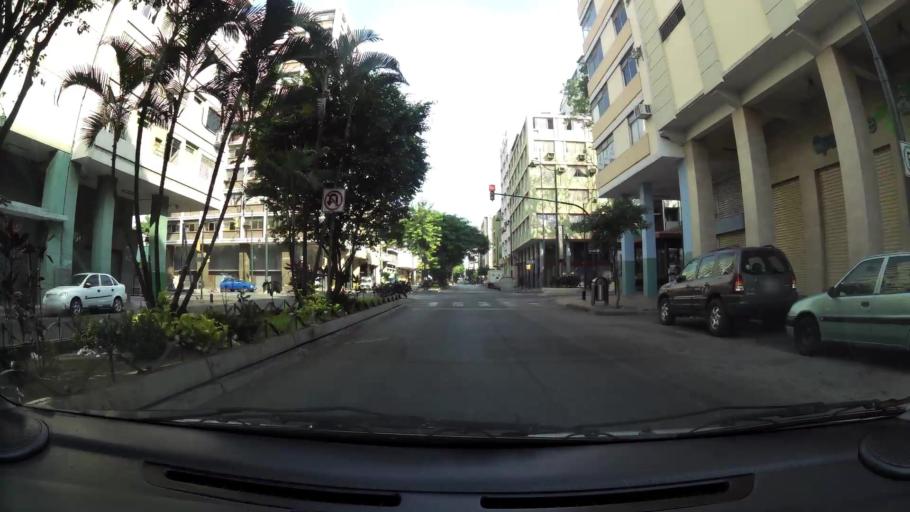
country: EC
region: Guayas
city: Guayaquil
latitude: -2.1970
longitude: -79.8822
